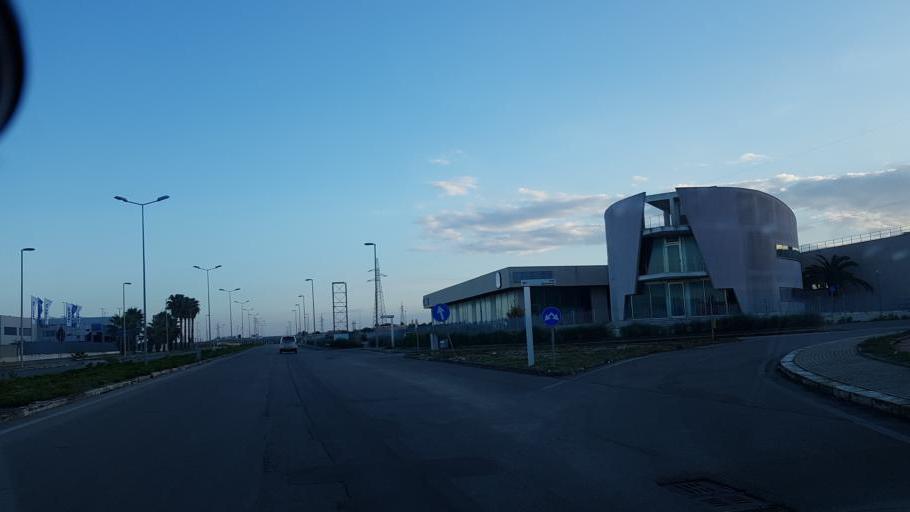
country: IT
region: Apulia
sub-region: Provincia di Lecce
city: Giorgilorio
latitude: 40.3735
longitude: 18.1364
